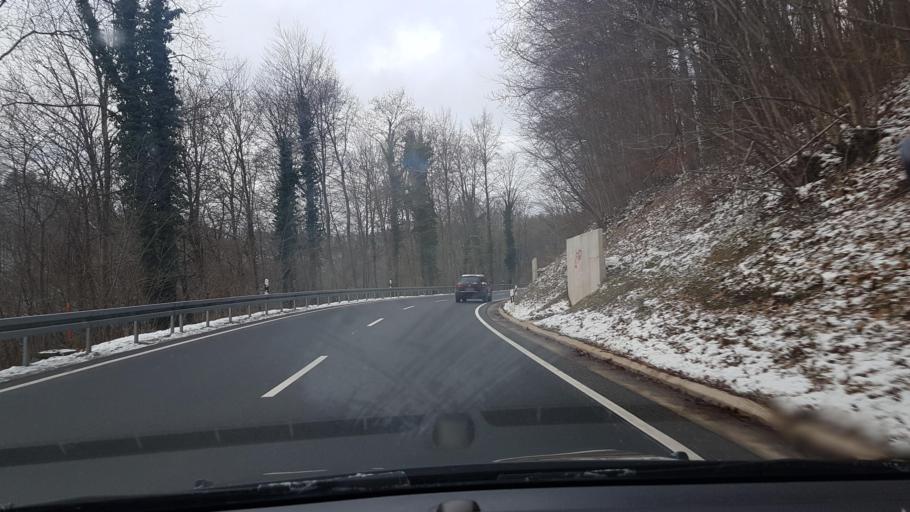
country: DE
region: Lower Saxony
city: Bad Grund
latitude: 51.8165
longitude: 10.2403
